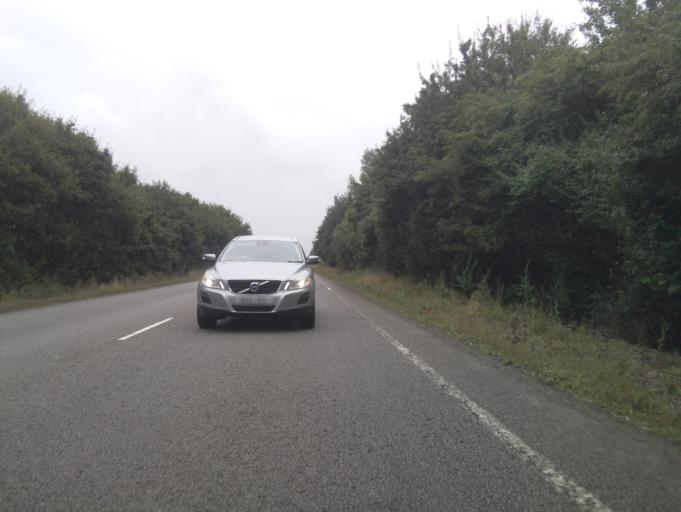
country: GB
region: England
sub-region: Nottinghamshire
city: South Collingham
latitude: 53.0913
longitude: -0.7656
